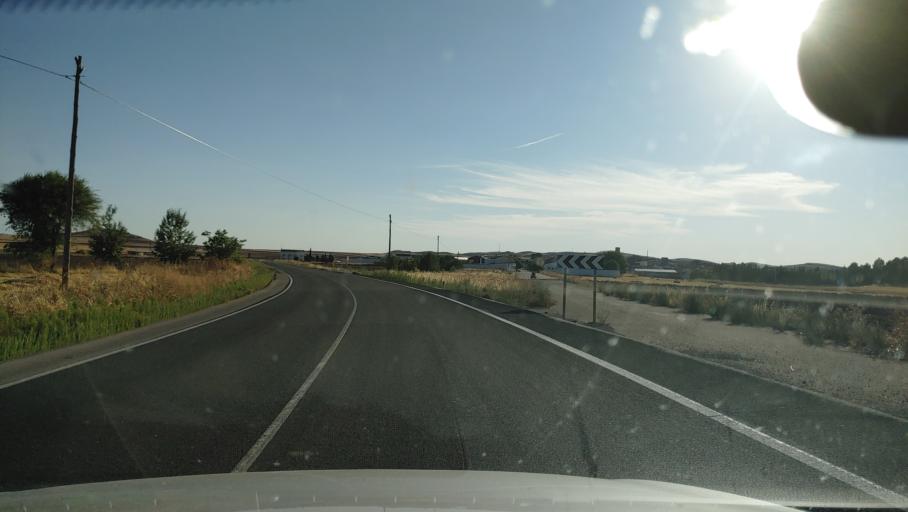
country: ES
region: Castille-La Mancha
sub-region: Provincia de Ciudad Real
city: Fuenllana
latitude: 38.7572
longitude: -2.9506
